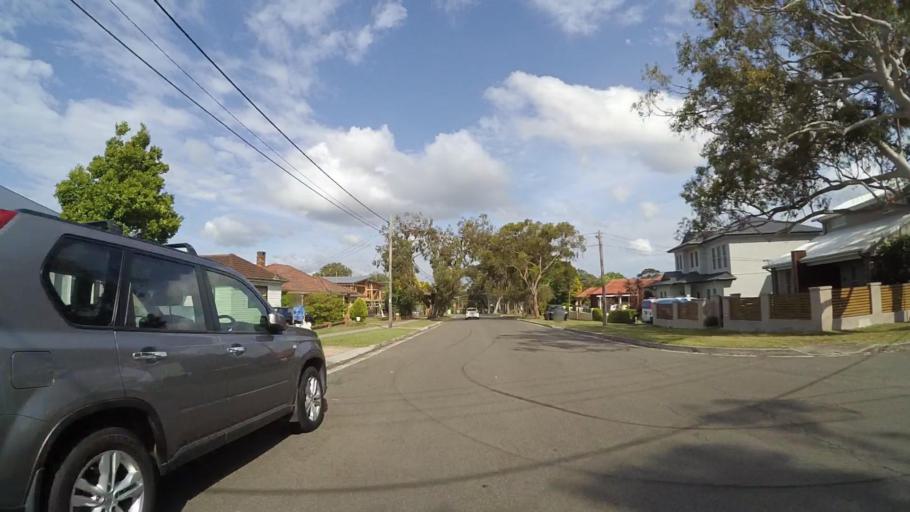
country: AU
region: New South Wales
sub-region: Sutherland Shire
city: Caringbah
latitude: -34.0458
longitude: 151.1157
